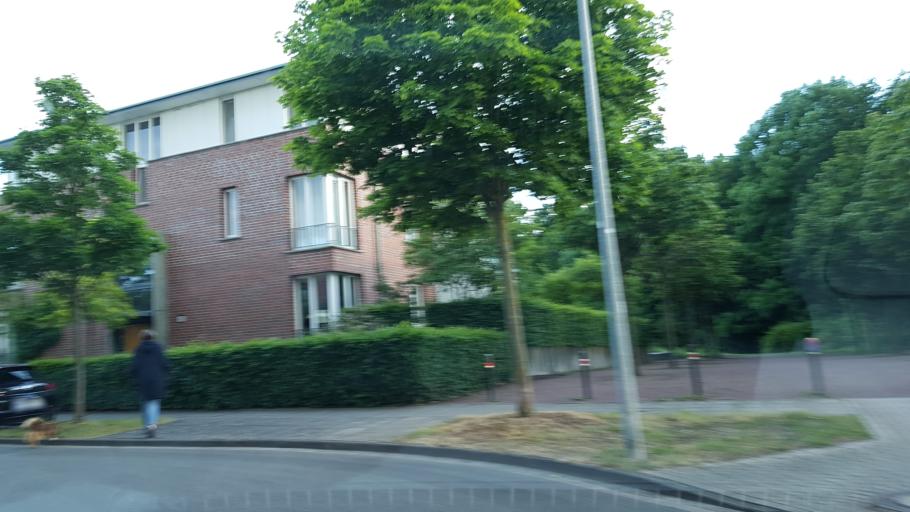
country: DE
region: Lower Saxony
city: Laatzen
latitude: 52.3475
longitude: 9.8089
